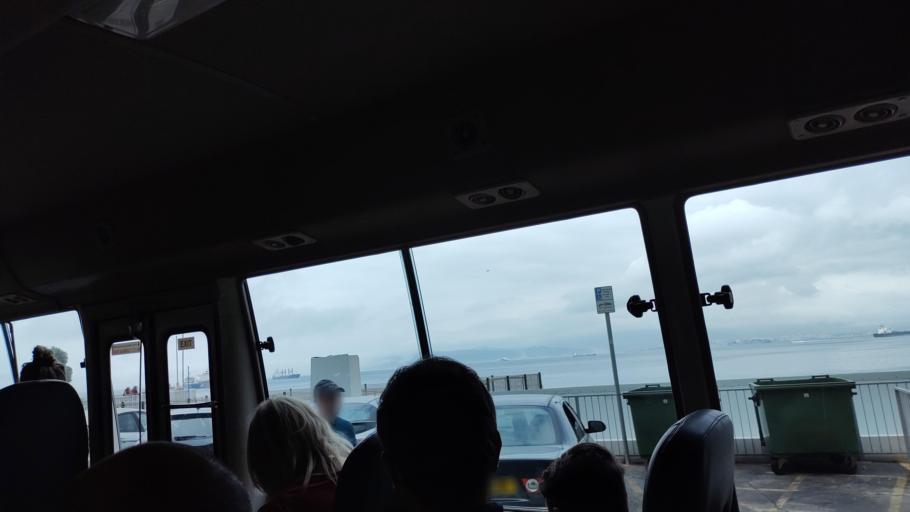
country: GI
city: Gibraltar
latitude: 36.1191
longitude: -5.3504
